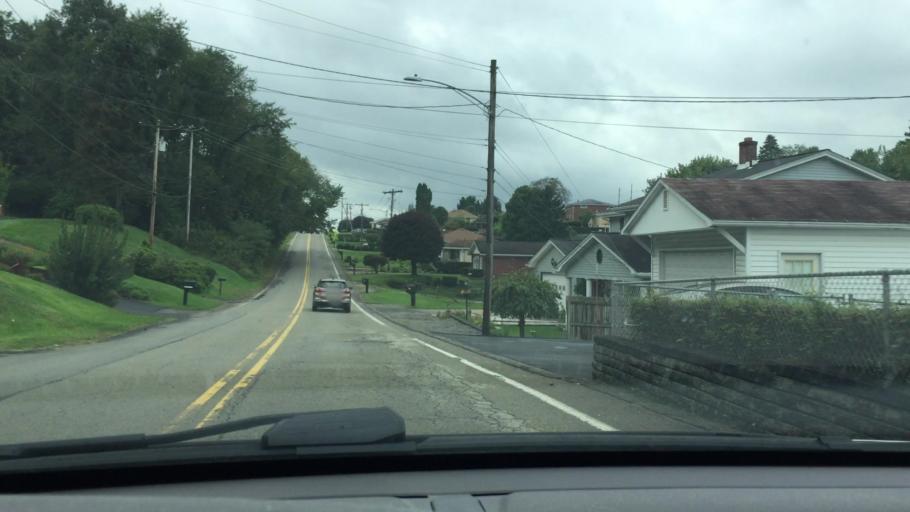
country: US
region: Pennsylvania
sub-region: Westmoreland County
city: North Belle Vernon
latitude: 40.1426
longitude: -79.8719
